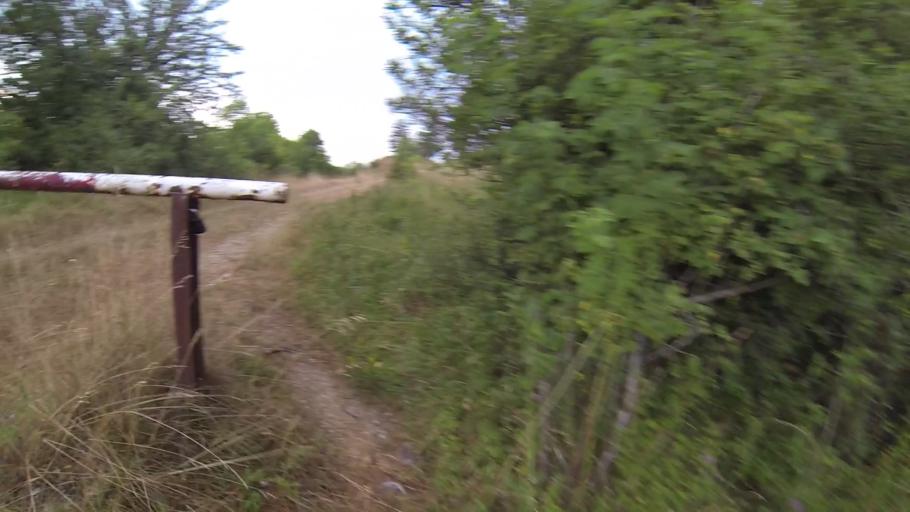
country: DE
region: Baden-Wuerttemberg
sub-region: Regierungsbezirk Stuttgart
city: Heidenheim an der Brenz
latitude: 48.6970
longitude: 10.1785
